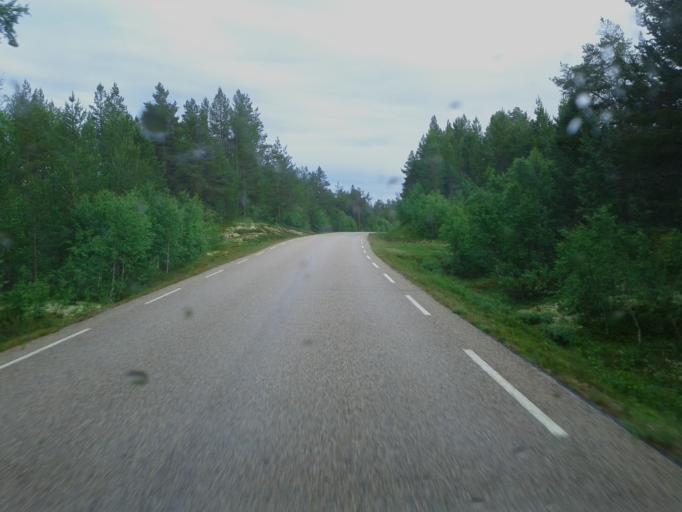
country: NO
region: Hedmark
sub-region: Engerdal
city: Engerdal
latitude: 62.0728
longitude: 11.6754
